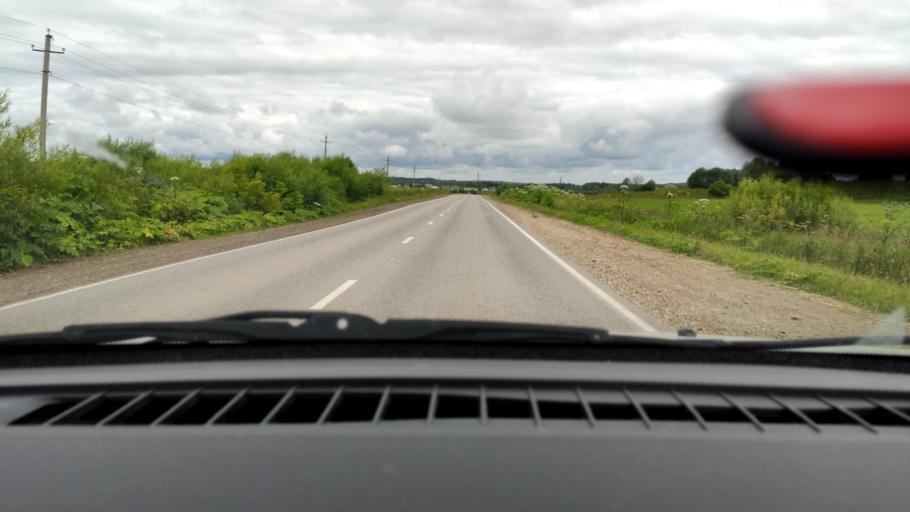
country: RU
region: Perm
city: Ust'-Kachka
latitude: 58.0716
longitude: 55.6247
